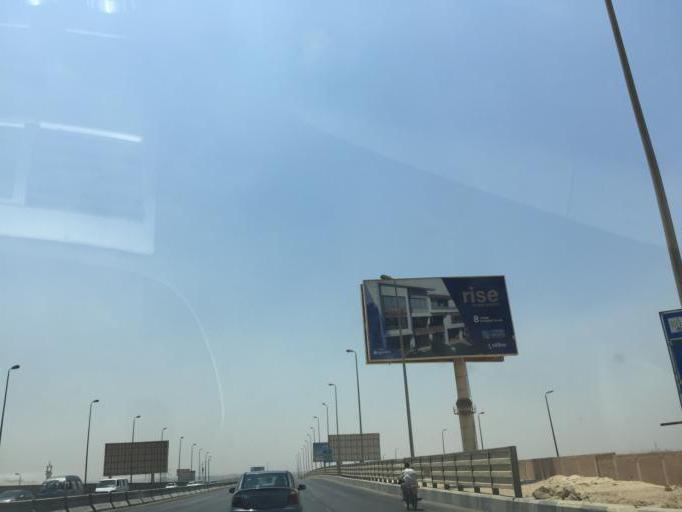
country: EG
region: Al Jizah
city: Awsim
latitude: 30.0502
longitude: 31.0595
